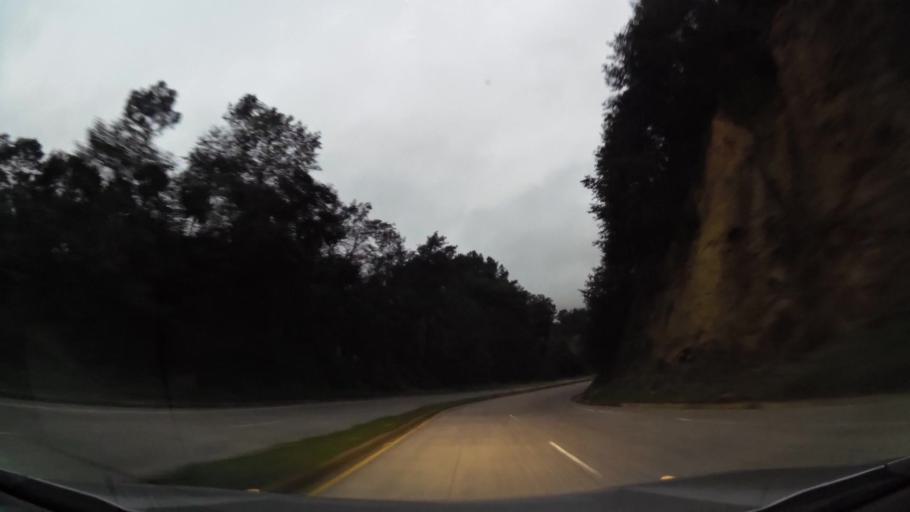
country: GT
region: Chimaltenango
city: Tecpan Guatemala
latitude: 14.8261
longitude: -91.0348
